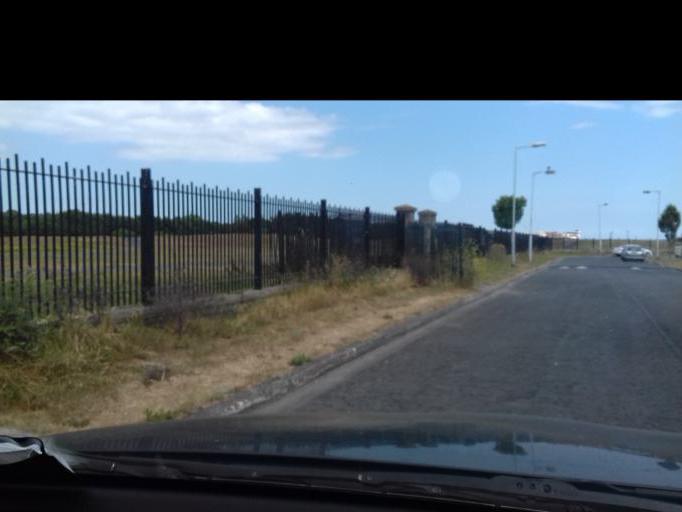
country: IE
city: Darndale
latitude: 53.4048
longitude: -6.1966
